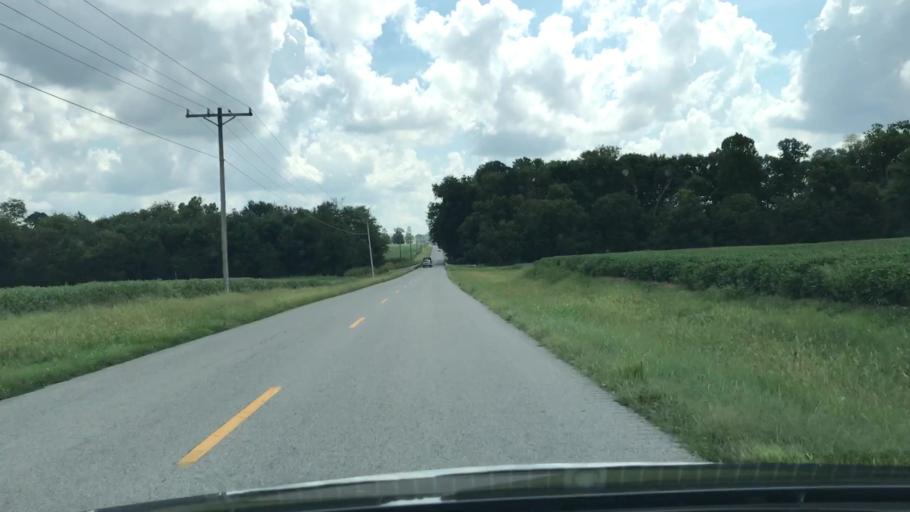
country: US
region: Kentucky
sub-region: Todd County
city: Elkton
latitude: 36.7235
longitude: -87.0839
